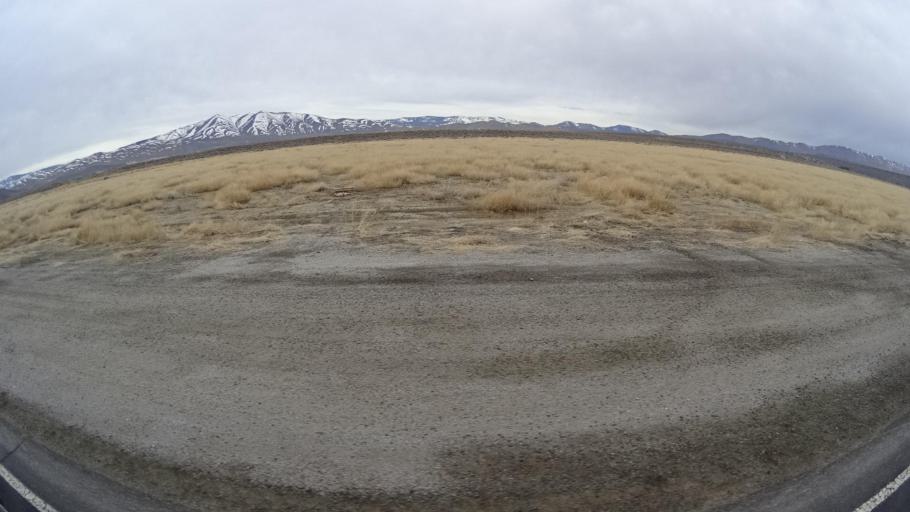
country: US
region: Nevada
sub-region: Washoe County
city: Lemmon Valley
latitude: 39.6618
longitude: -119.8286
